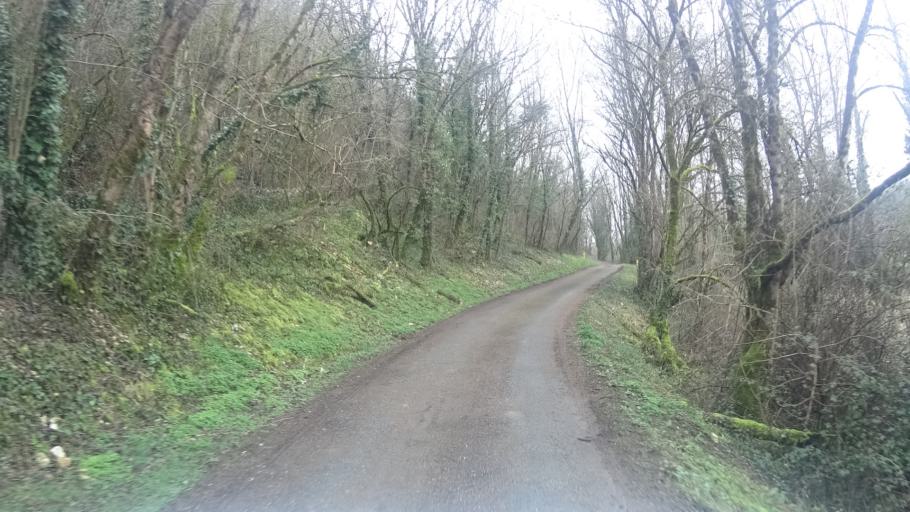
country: FR
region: Aquitaine
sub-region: Departement de la Dordogne
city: Terrasson-Lavilledieu
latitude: 45.1087
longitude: 1.2393
